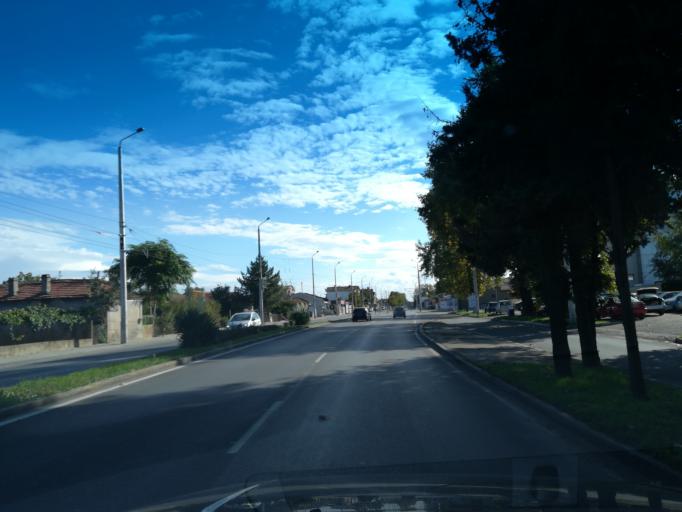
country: BG
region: Stara Zagora
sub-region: Obshtina Stara Zagora
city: Stara Zagora
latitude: 42.4027
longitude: 25.6429
